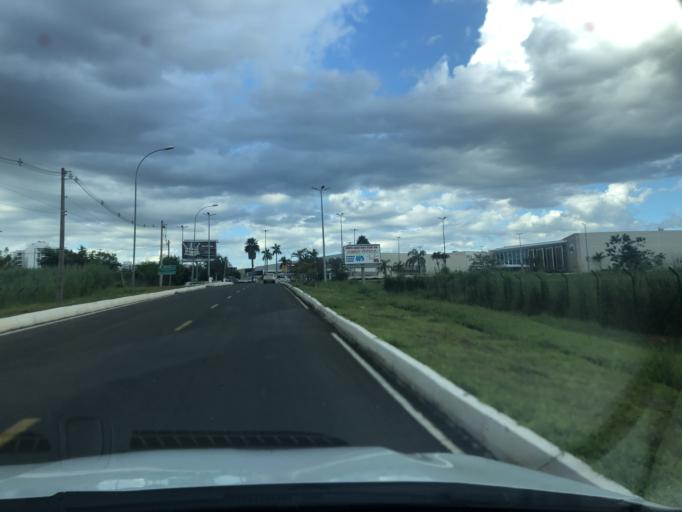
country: BR
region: Federal District
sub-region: Brasilia
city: Brasilia
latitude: -15.8347
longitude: -47.9579
